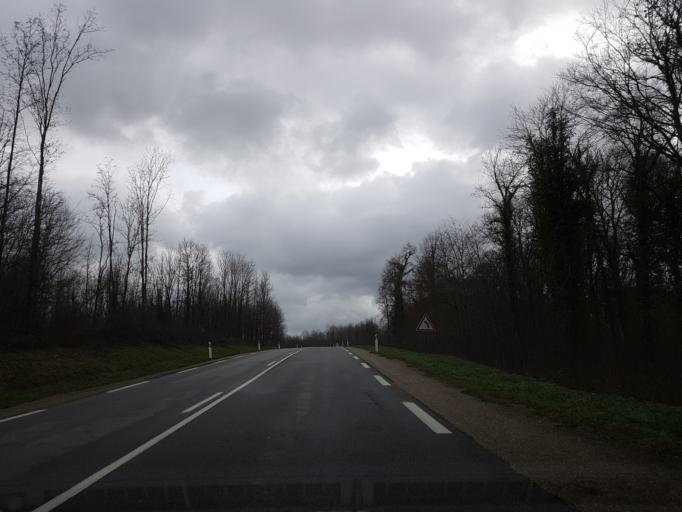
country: FR
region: Champagne-Ardenne
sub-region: Departement de la Haute-Marne
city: Fayl-Billot
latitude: 47.7984
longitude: 5.5629
